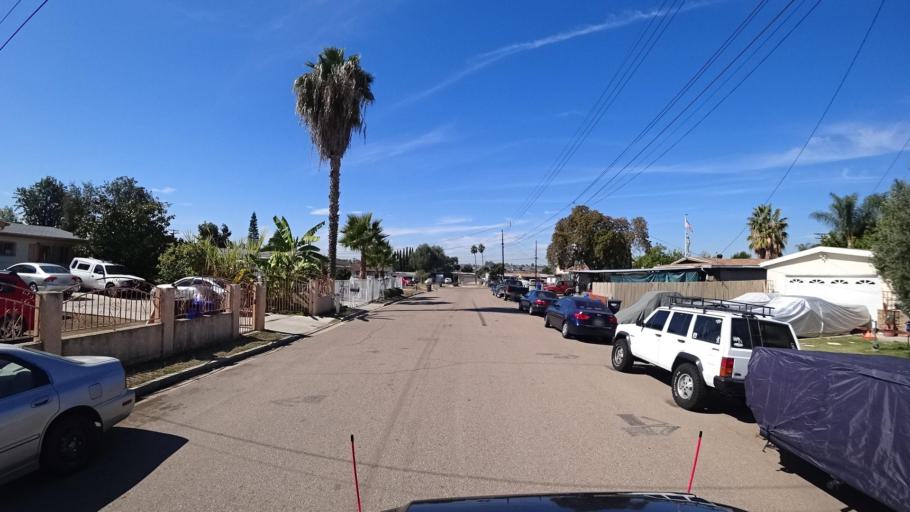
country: US
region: California
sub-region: San Diego County
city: La Presa
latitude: 32.7036
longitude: -117.0032
